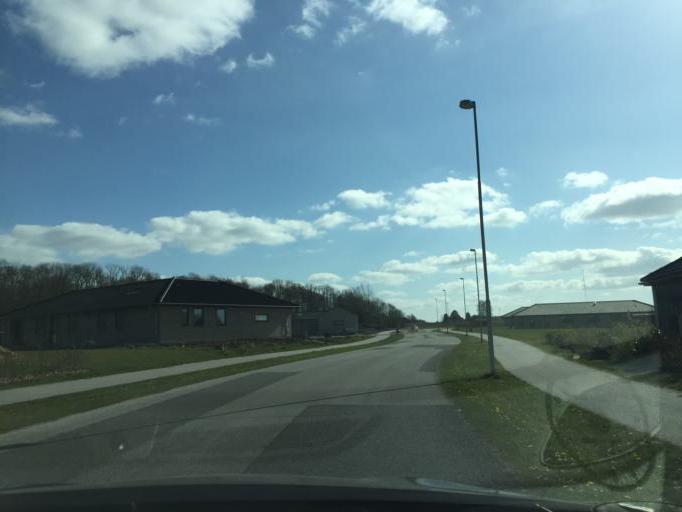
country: DK
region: South Denmark
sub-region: Faaborg-Midtfyn Kommune
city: Arslev
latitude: 55.3040
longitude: 10.4975
